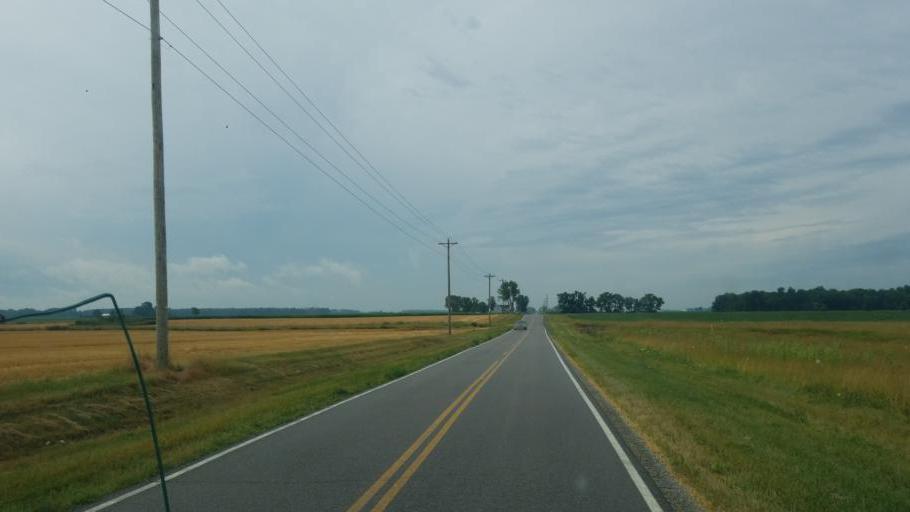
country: US
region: Ohio
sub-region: Defiance County
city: Hicksville
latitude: 41.3351
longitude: -84.6899
